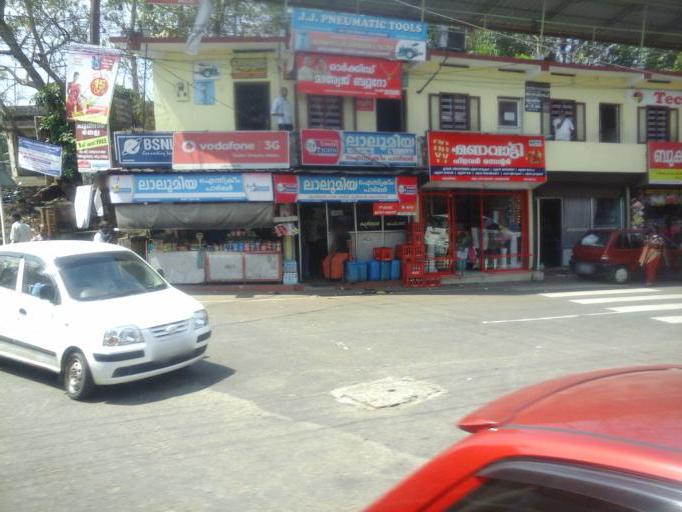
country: IN
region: Kerala
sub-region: Kottayam
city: Erattupetta
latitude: 9.6861
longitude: 76.7772
